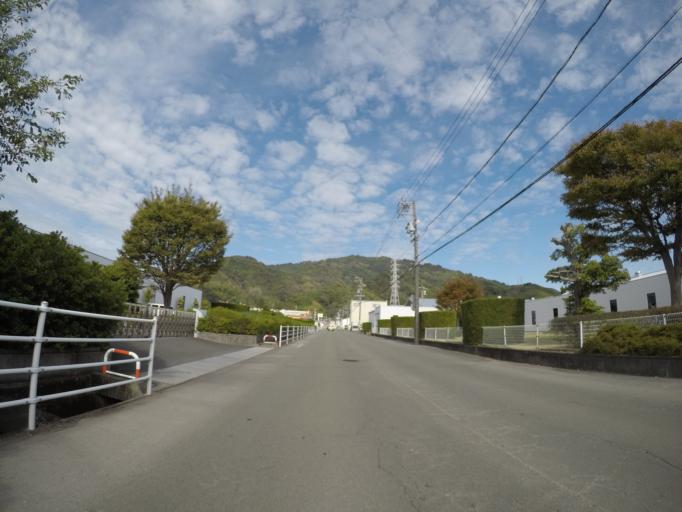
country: JP
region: Shizuoka
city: Yaizu
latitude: 34.8882
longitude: 138.3095
